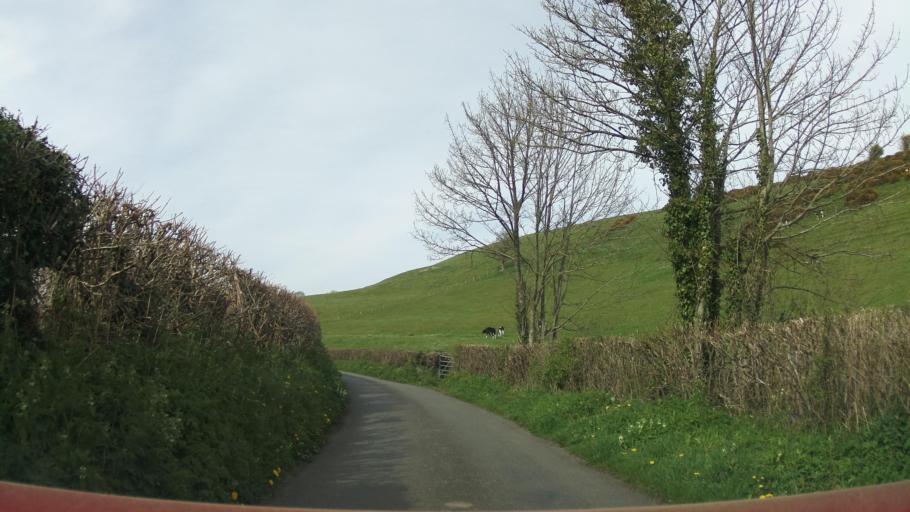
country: GB
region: England
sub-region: Somerset
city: Milborne Port
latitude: 50.9687
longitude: -2.4909
